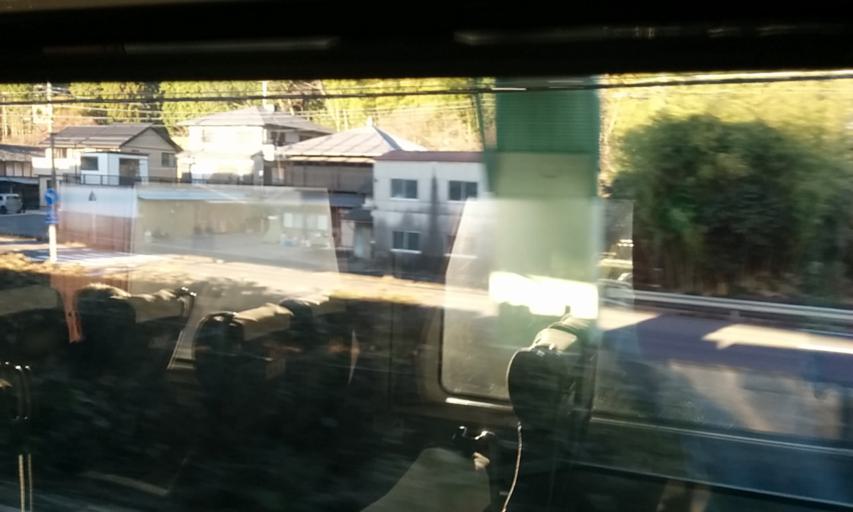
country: JP
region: Gifu
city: Mizunami
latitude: 35.3649
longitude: 137.2261
